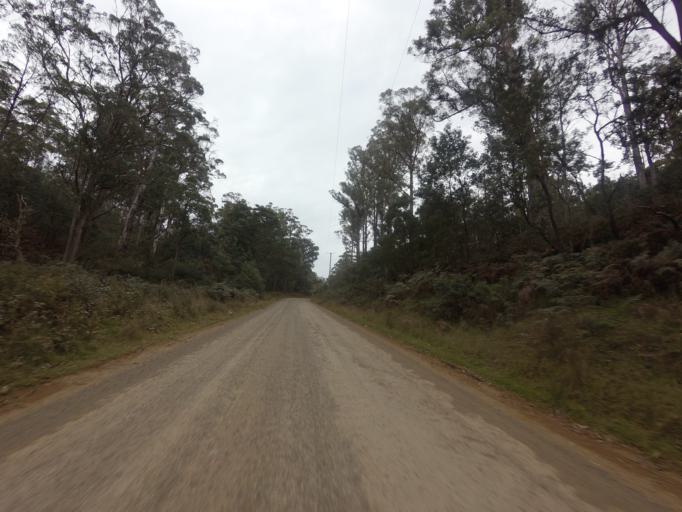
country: AU
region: Tasmania
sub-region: Derwent Valley
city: New Norfolk
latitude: -42.5840
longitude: 147.0096
